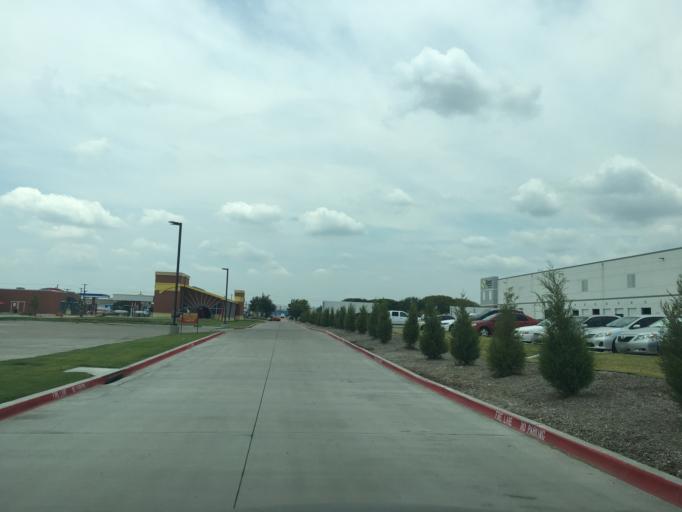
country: US
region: Texas
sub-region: Dallas County
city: Garland
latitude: 32.8959
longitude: -96.6806
